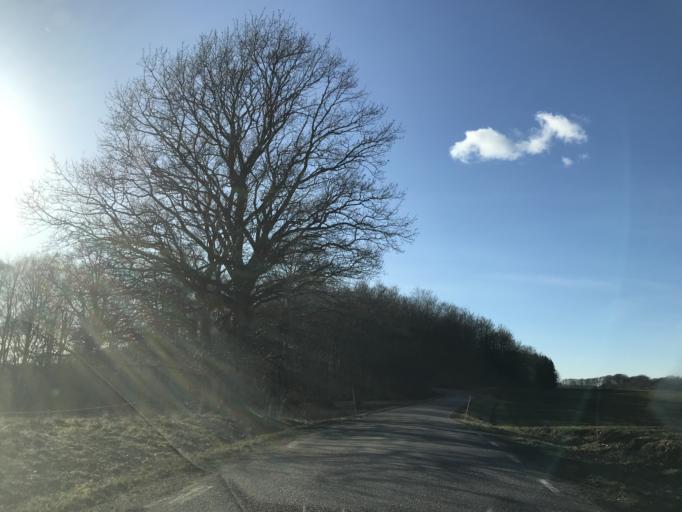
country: SE
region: Skane
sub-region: Ystads Kommun
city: Ystad
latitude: 55.5473
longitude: 13.7986
